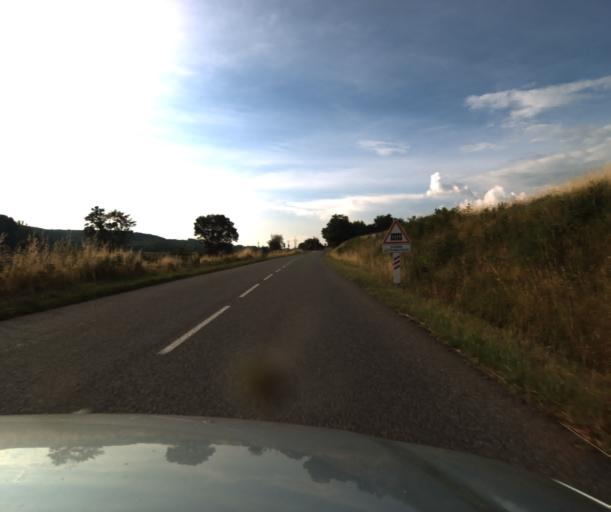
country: FR
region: Midi-Pyrenees
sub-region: Departement du Tarn-et-Garonne
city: Saint-Porquier
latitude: 43.9771
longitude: 1.1266
